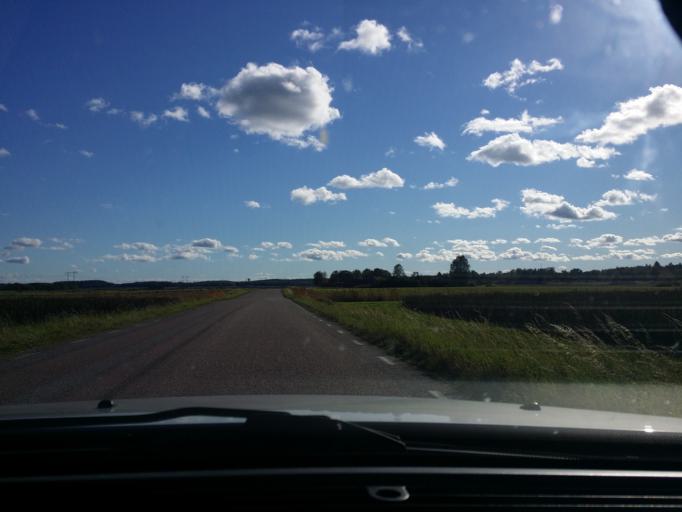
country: SE
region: Soedermanland
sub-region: Eskilstuna Kommun
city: Torshalla
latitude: 59.5399
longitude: 16.4481
